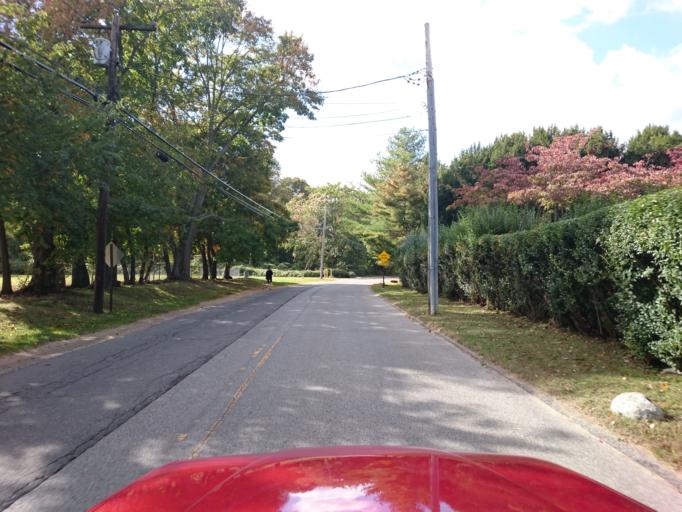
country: US
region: New York
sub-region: Nassau County
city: Glen Cove
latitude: 40.8836
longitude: -73.6251
